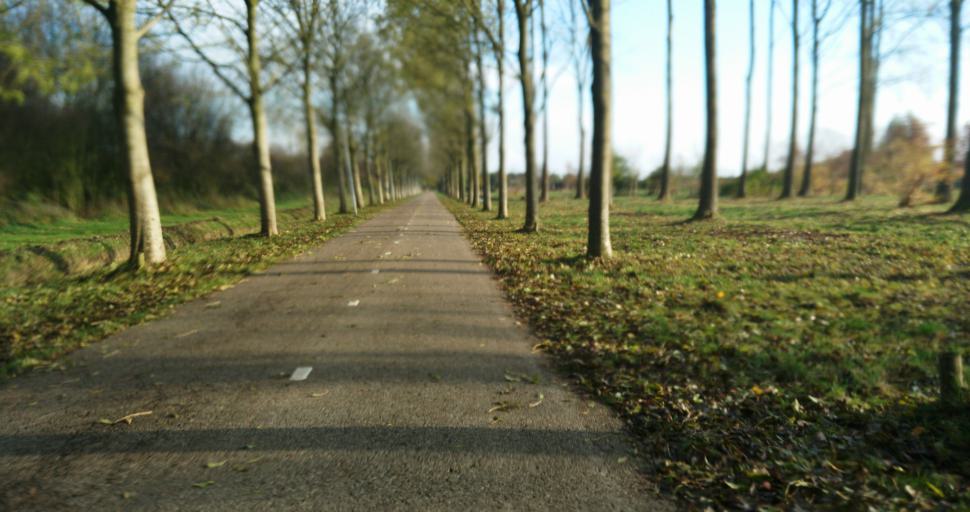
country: NL
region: Groningen
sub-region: Gemeente Groningen
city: Oosterpark
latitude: 53.2419
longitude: 6.5941
